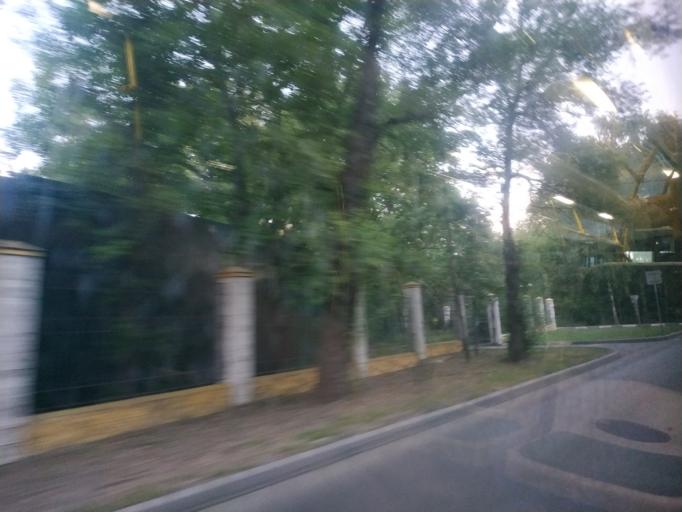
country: RU
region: Moskovskaya
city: Mosrentgen
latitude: 55.6169
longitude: 37.4747
